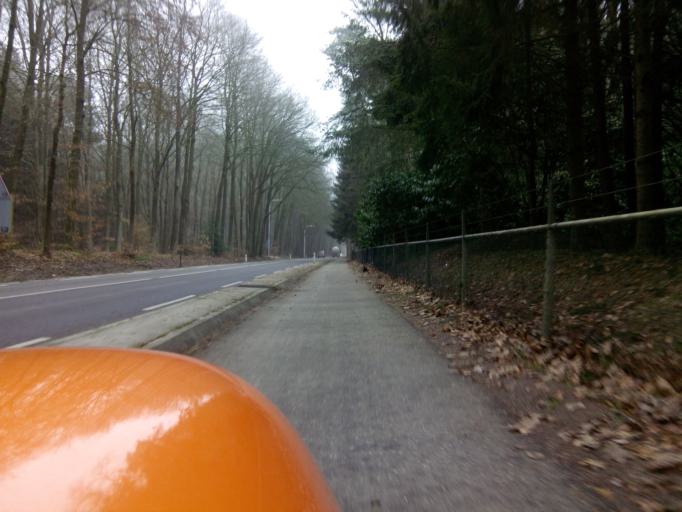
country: NL
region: Gelderland
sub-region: Gemeente Barneveld
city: Garderen
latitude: 52.2373
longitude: 5.6592
